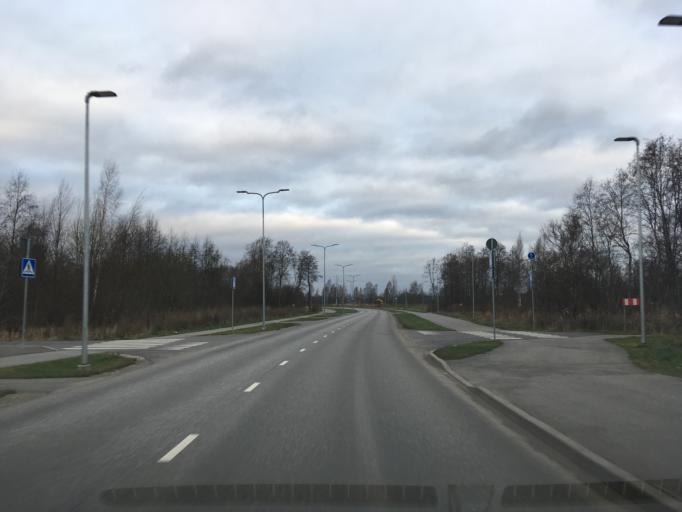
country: EE
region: Paernumaa
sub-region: Paernu linn
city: Parnu
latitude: 58.3991
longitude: 24.4817
